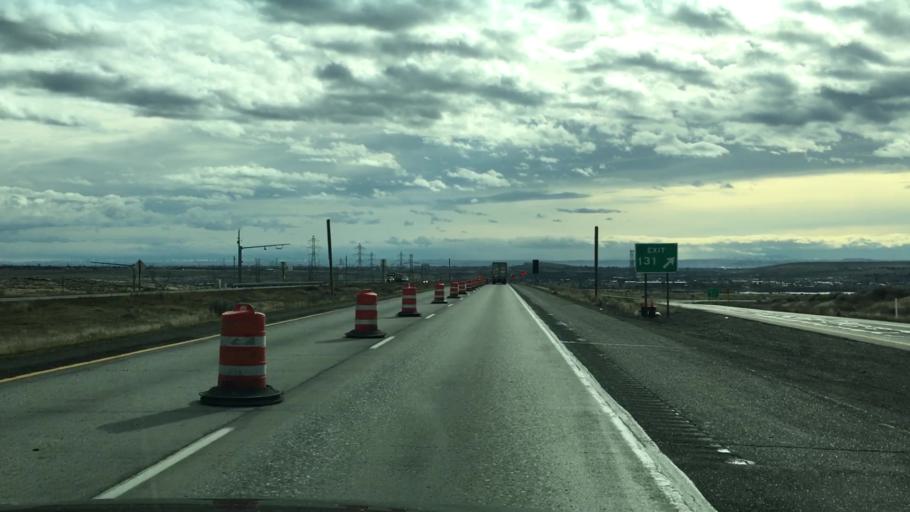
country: US
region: Oregon
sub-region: Umatilla County
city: Umatilla
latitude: 45.9485
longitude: -119.3369
